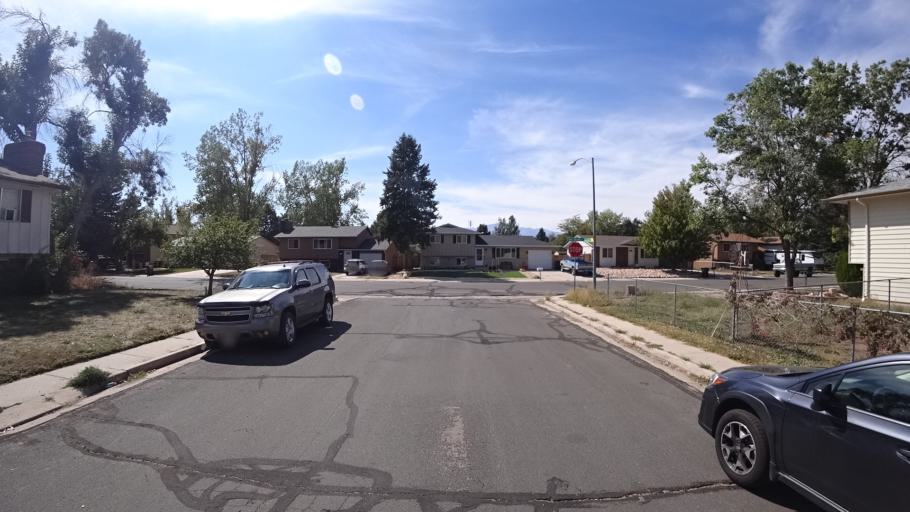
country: US
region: Colorado
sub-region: El Paso County
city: Cimarron Hills
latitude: 38.8973
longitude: -104.7567
